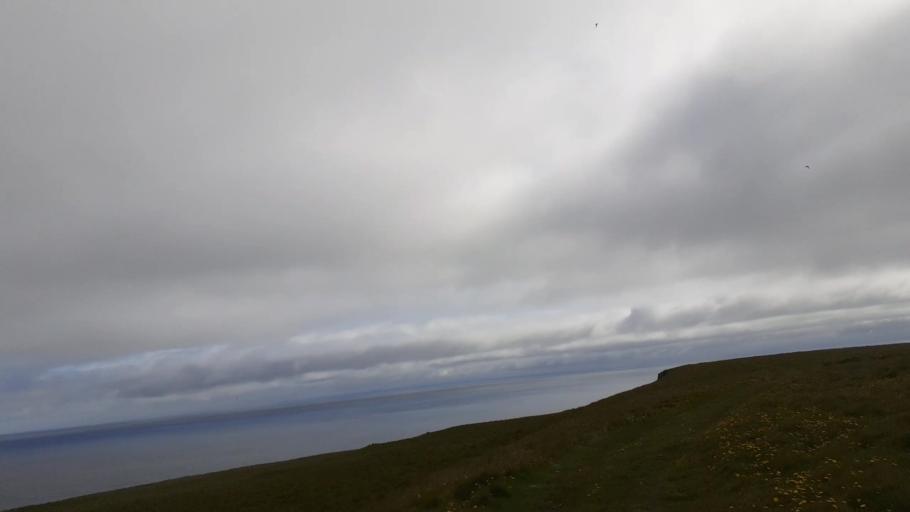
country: IS
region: Northeast
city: Dalvik
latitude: 66.5397
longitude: -17.9833
